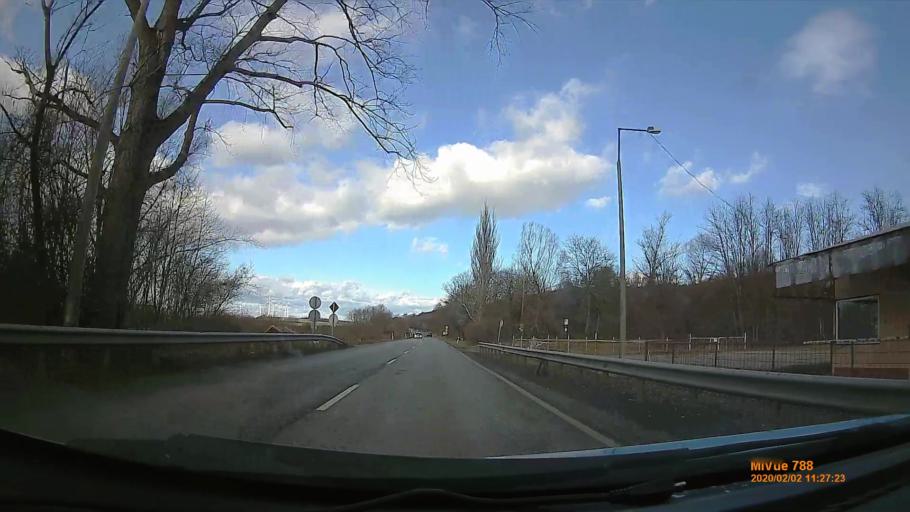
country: HU
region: Gyor-Moson-Sopron
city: Sopron
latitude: 47.7172
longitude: 16.5694
